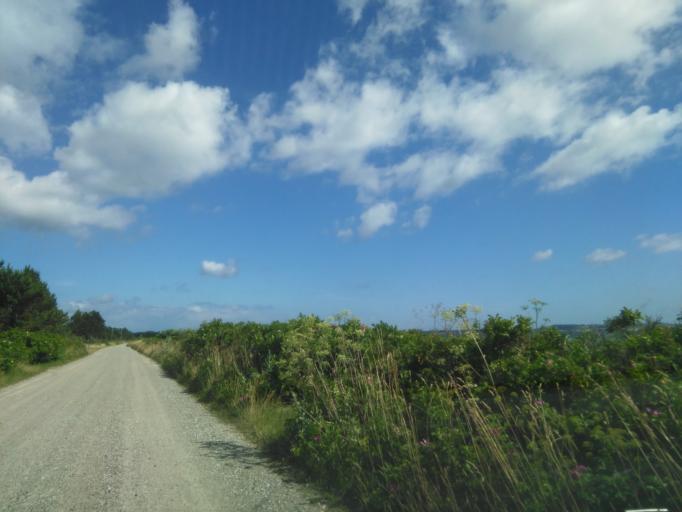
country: DK
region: Central Jutland
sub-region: Syddjurs Kommune
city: Ronde
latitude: 56.1818
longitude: 10.4581
